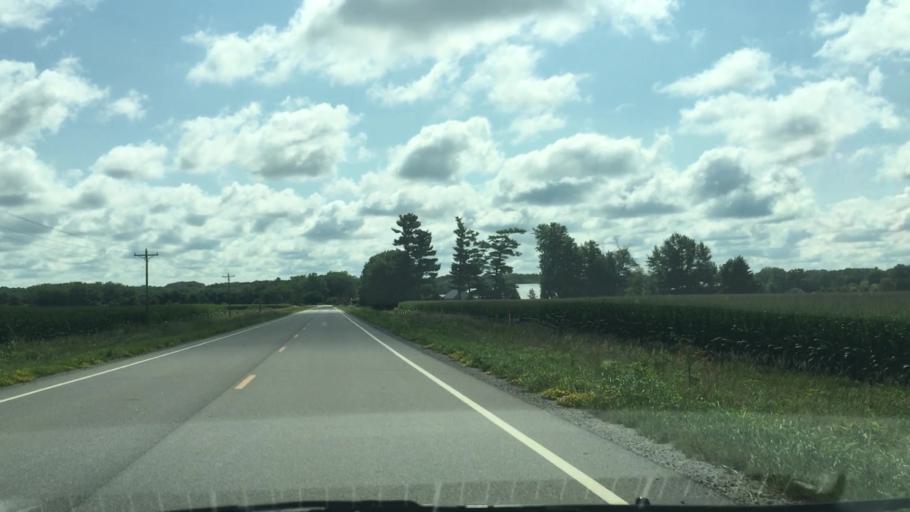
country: US
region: Iowa
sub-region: Linn County
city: Mount Vernon
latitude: 41.8414
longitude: -91.4057
